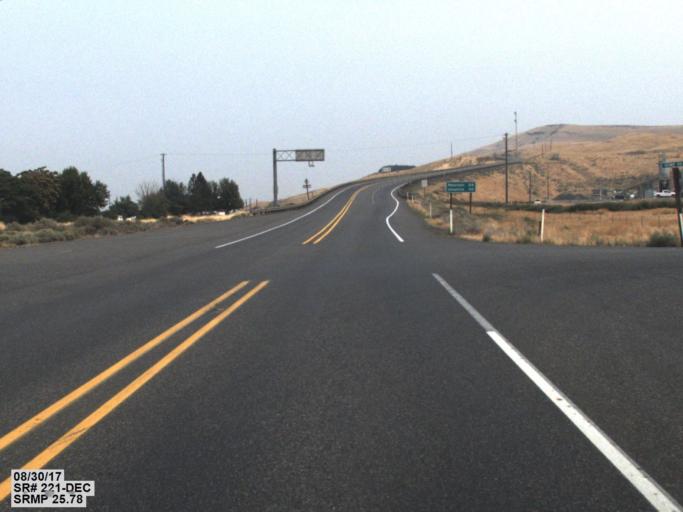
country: US
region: Washington
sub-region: Benton County
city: Prosser
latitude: 46.2069
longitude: -119.7428
